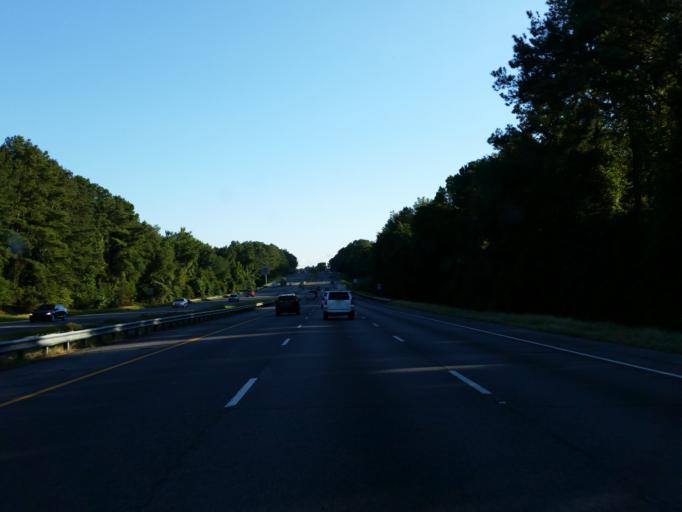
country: US
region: Georgia
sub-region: Houston County
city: Perry
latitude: 32.4216
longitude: -83.7602
